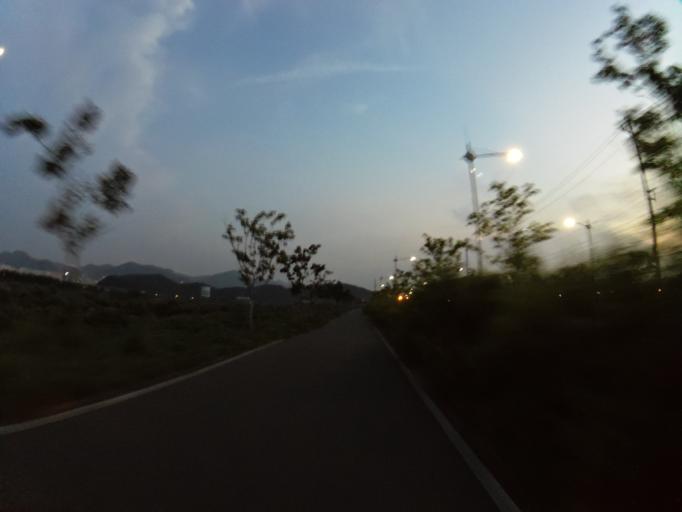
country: KR
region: Gyeongsangbuk-do
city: Gyeongsan-si
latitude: 35.8613
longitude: 128.7091
